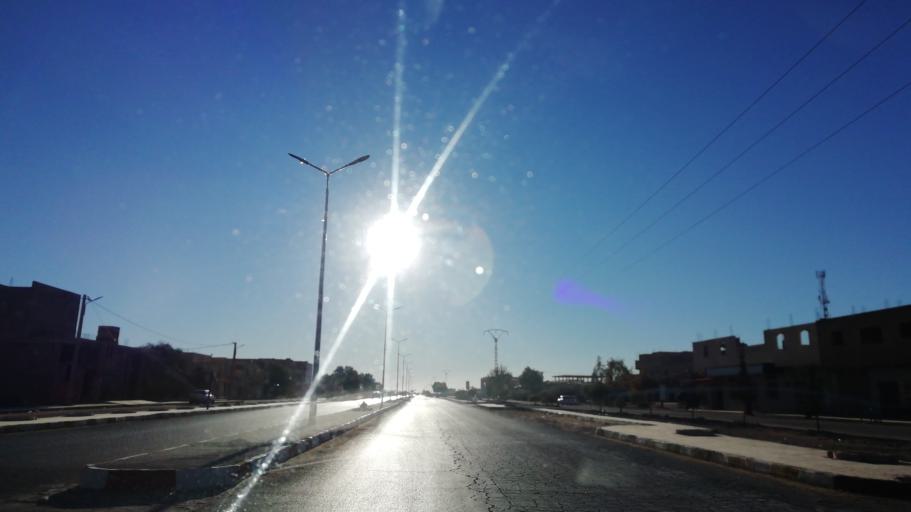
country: DZ
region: Saida
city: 'Ain el Hadjar
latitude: 34.0285
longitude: 0.0936
